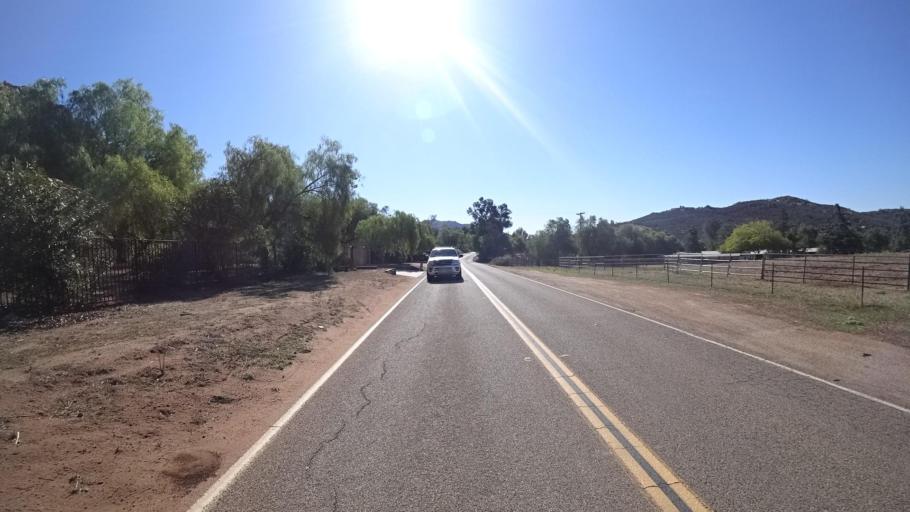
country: US
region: California
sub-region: San Diego County
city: Jamul
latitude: 32.7213
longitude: -116.8051
